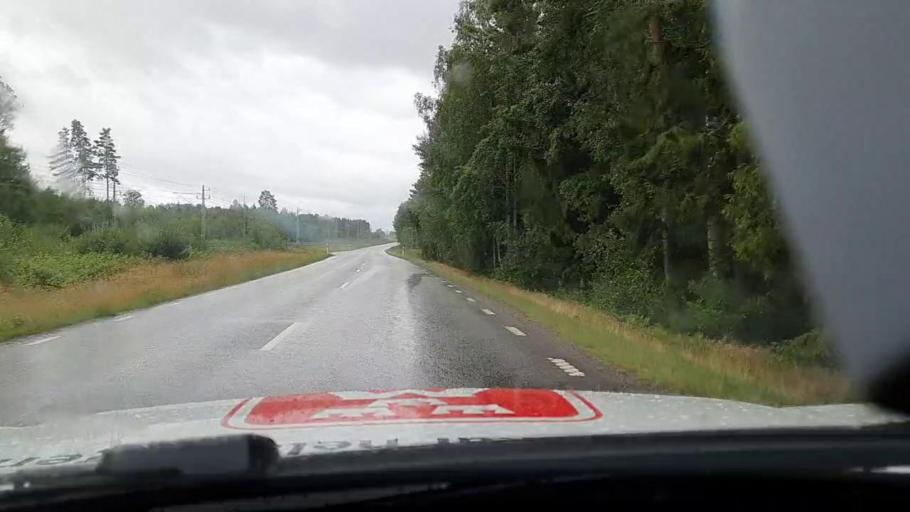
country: SE
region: Vaestra Goetaland
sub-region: Toreboda Kommun
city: Toereboda
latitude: 58.6646
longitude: 14.0906
